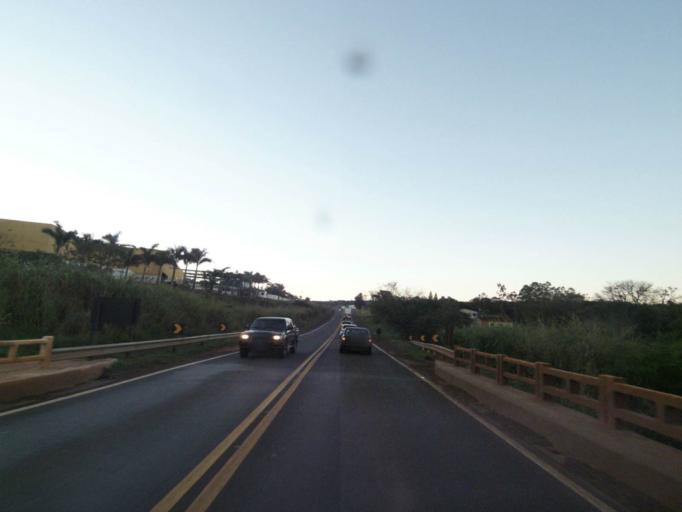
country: BR
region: Parana
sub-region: Londrina
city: Londrina
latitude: -23.4008
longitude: -51.1336
